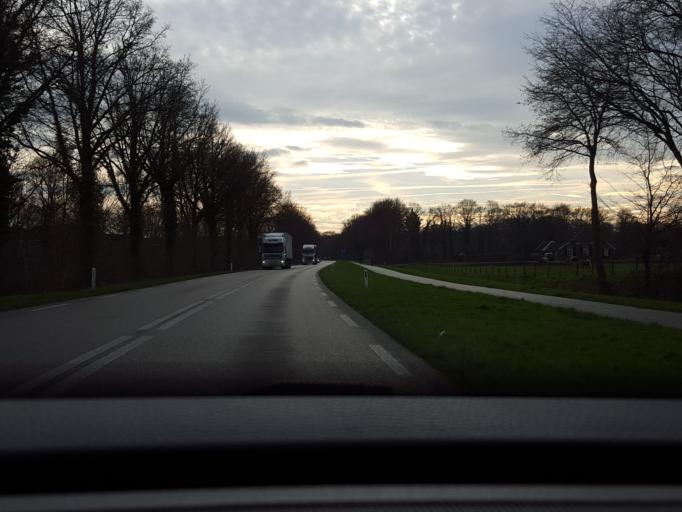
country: NL
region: Gelderland
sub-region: Gemeente Lochem
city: Almen
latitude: 52.1079
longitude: 6.2984
